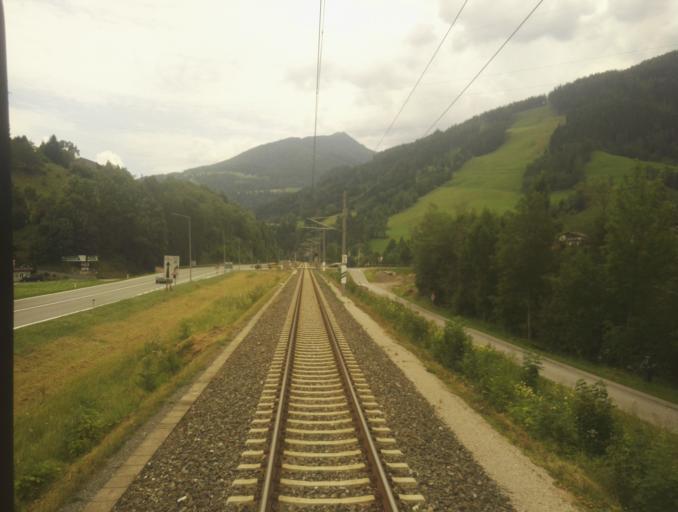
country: AT
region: Salzburg
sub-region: Politischer Bezirk Sankt Johann im Pongau
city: Forstau
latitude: 47.3920
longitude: 13.5947
